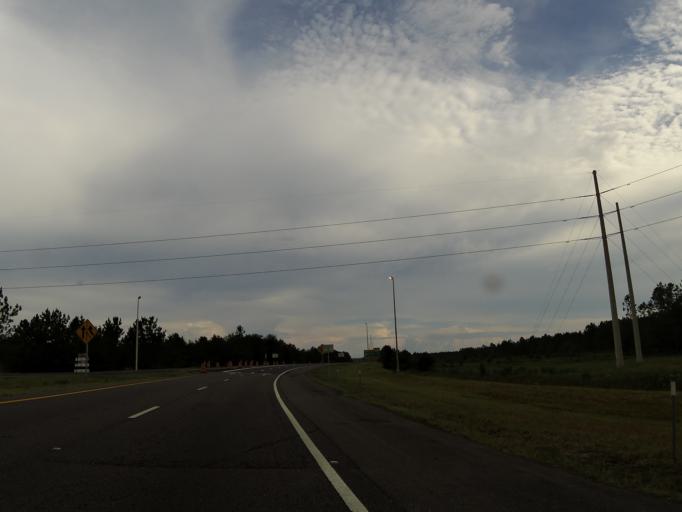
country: US
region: Florida
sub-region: Duval County
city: Baldwin
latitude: 30.2985
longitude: -81.8794
